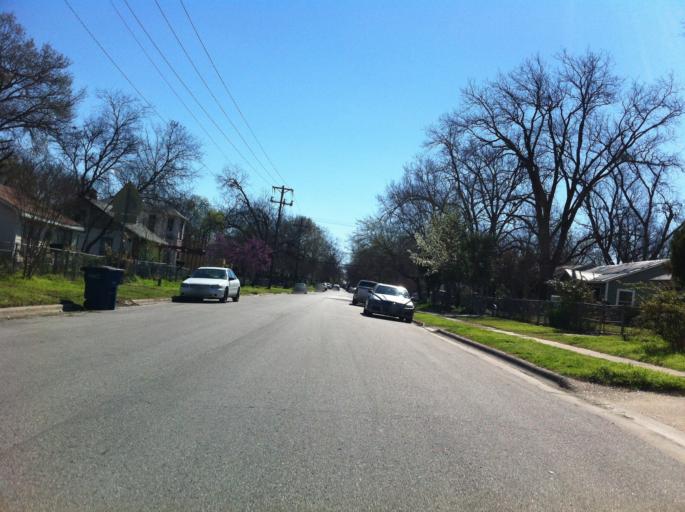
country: US
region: Texas
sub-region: Travis County
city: Austin
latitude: 30.2530
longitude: -97.7280
